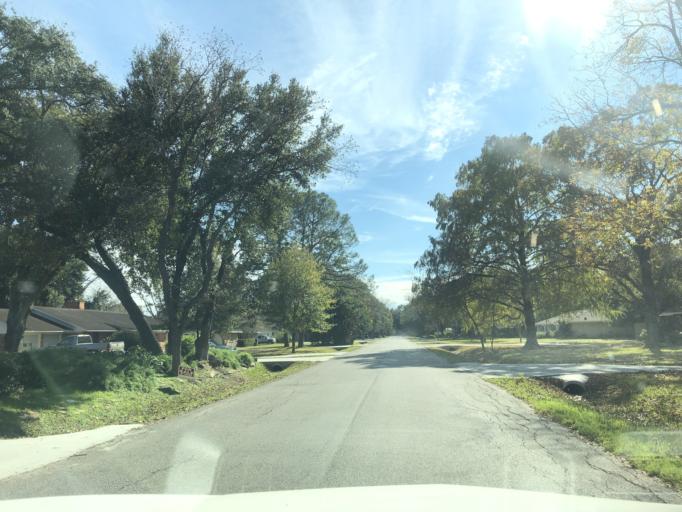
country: US
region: Texas
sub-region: Harris County
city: Bellaire
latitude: 29.6824
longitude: -95.5130
